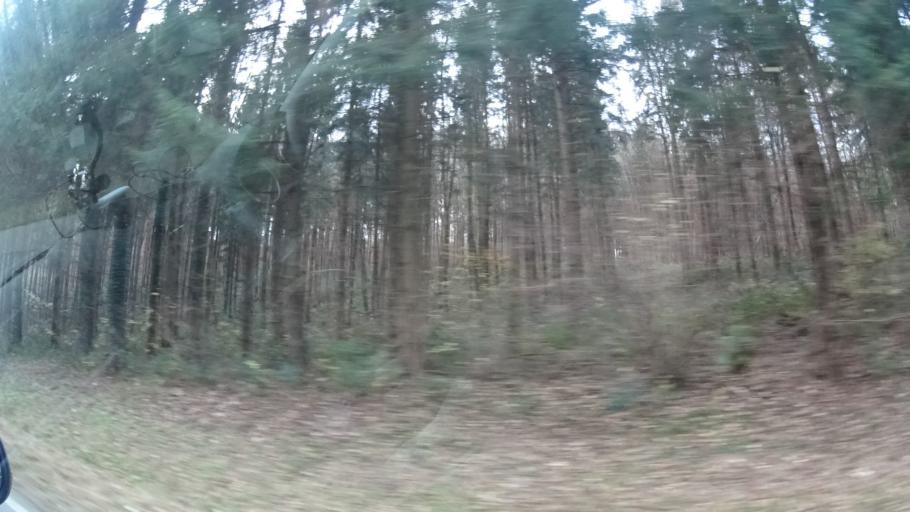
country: DE
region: Baden-Wuerttemberg
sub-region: Karlsruhe Region
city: Wiesenbach
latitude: 49.3618
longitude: 8.8409
